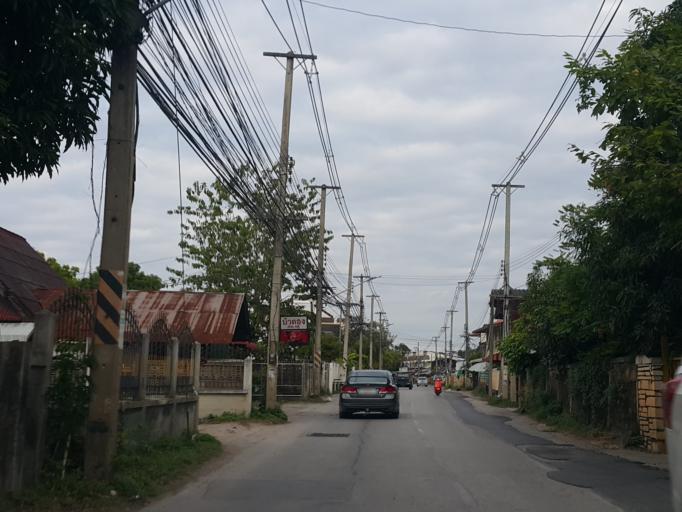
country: TH
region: Lampang
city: Lampang
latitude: 18.3015
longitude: 99.5064
